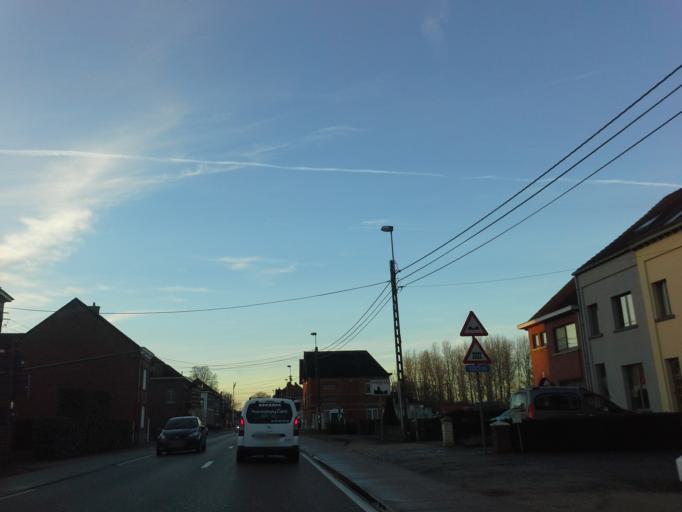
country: BE
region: Flanders
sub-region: Provincie Vlaams-Brabant
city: Scherpenheuvel-Zichem
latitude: 51.0073
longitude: 4.9900
